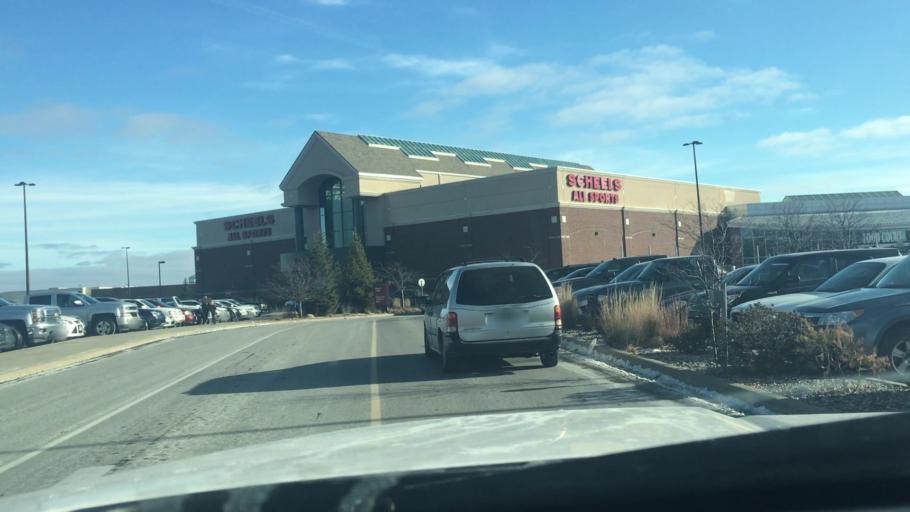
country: US
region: Minnesota
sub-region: Stearns County
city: Waite Park
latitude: 45.5561
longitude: -94.2135
